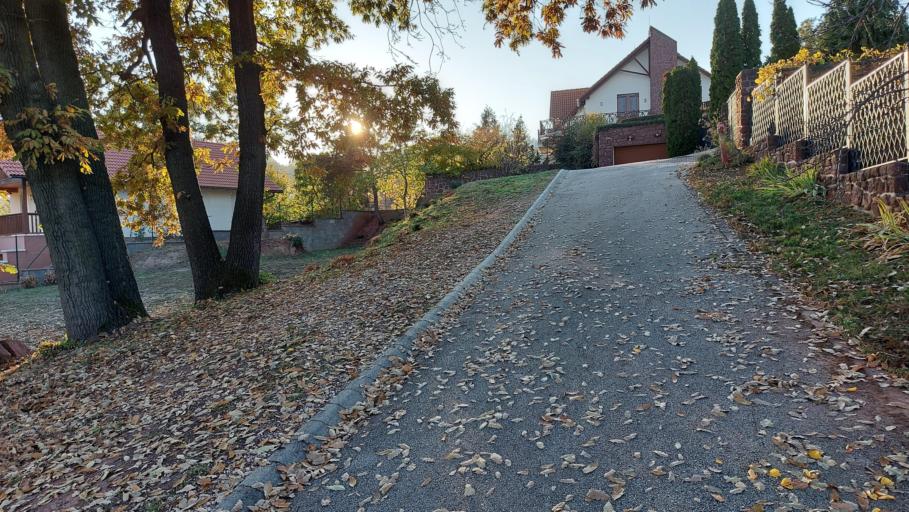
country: HU
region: Veszprem
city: Balatonalmadi
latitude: 47.0322
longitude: 18.0056
